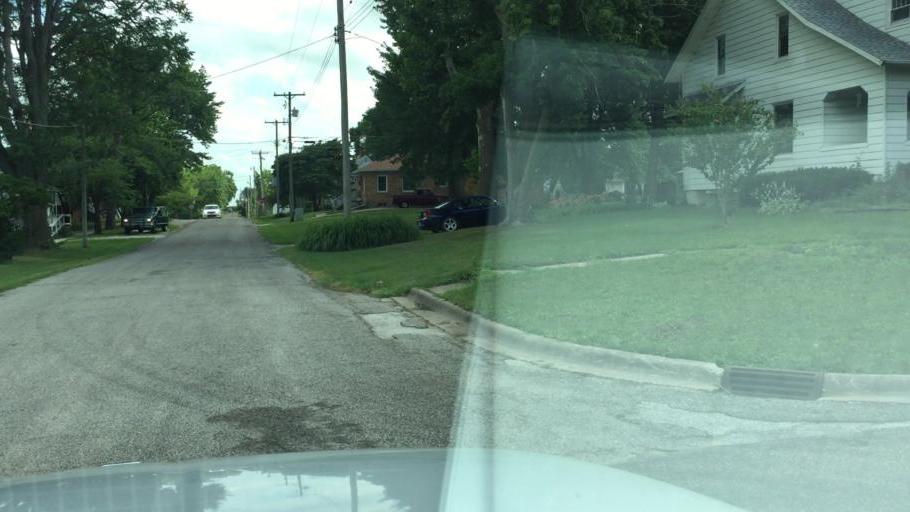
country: US
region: Illinois
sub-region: Hancock County
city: Carthage
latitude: 40.4136
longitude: -91.1275
